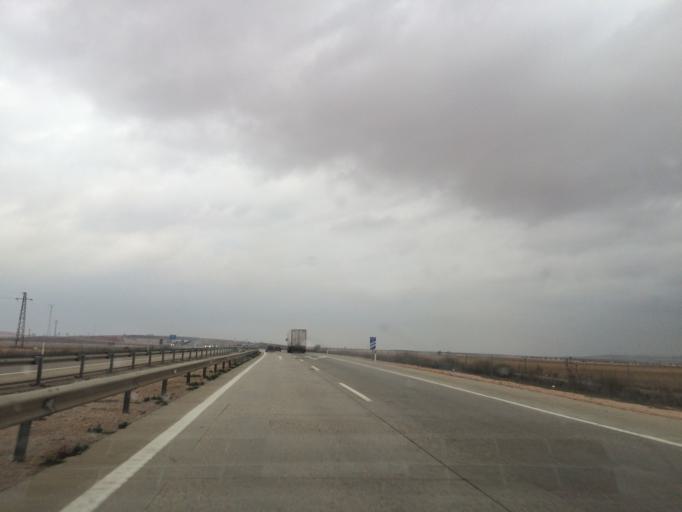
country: ES
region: Castille-La Mancha
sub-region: Province of Toledo
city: Madridejos
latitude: 39.5683
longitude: -3.5142
